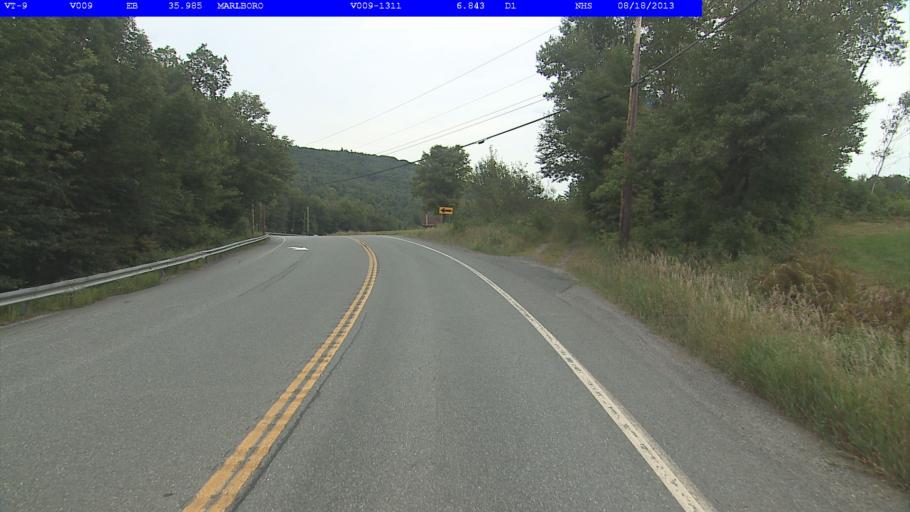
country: US
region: Vermont
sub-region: Windham County
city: West Brattleboro
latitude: 42.8795
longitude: -72.7028
